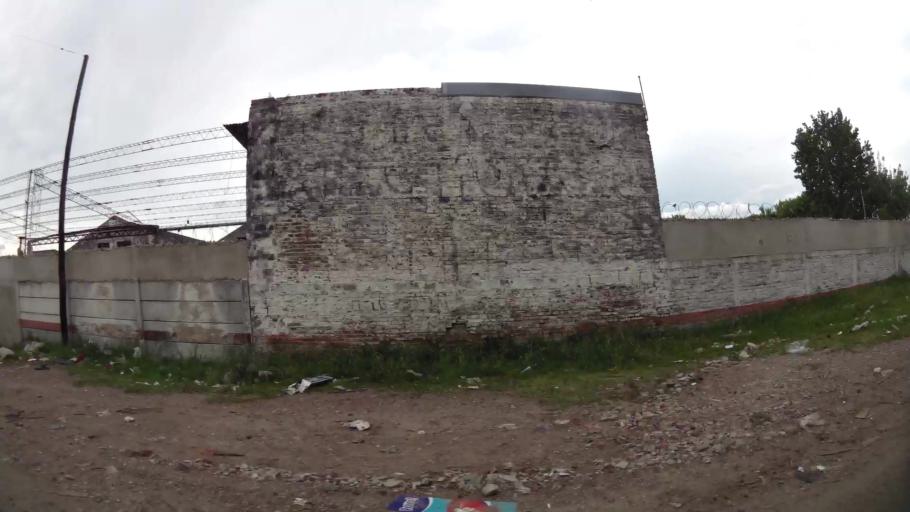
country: AR
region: Santa Fe
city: Gobernador Galvez
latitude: -32.9985
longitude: -60.6735
